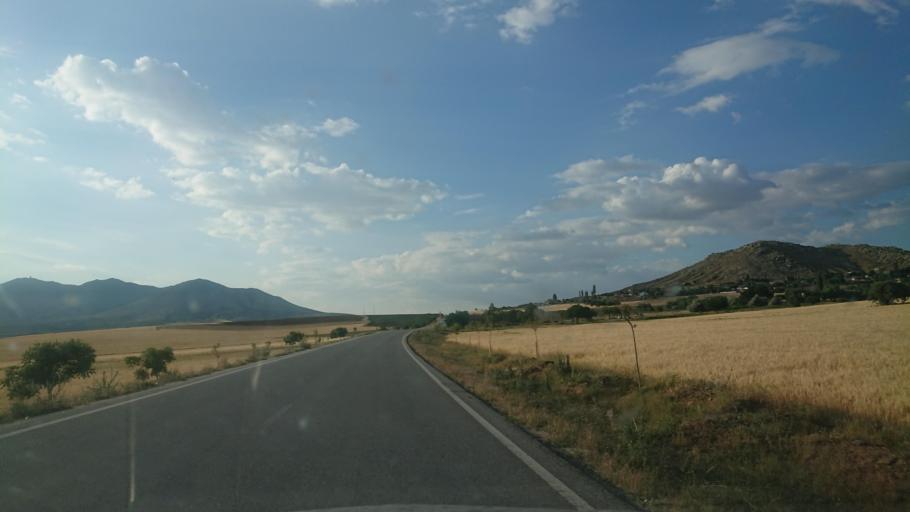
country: TR
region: Aksaray
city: Balci
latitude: 38.5844
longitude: 34.1028
